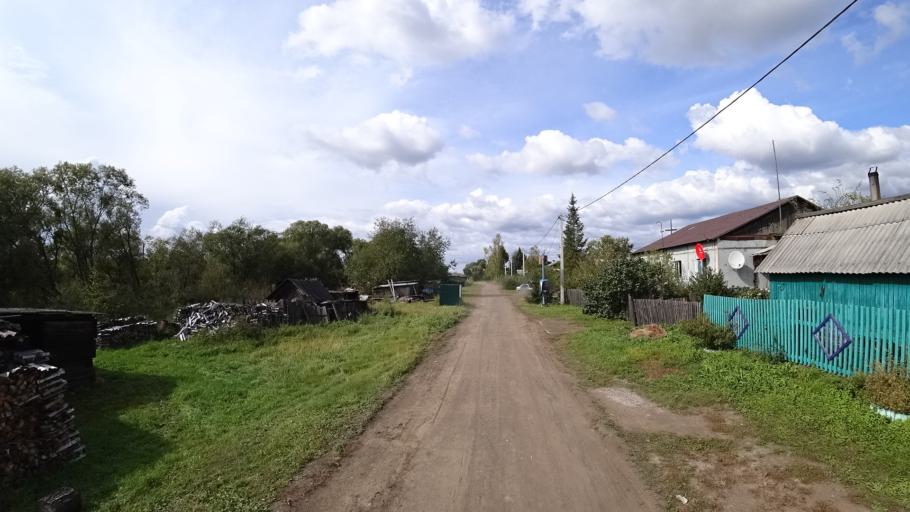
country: RU
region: Amur
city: Arkhara
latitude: 49.3528
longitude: 130.1583
